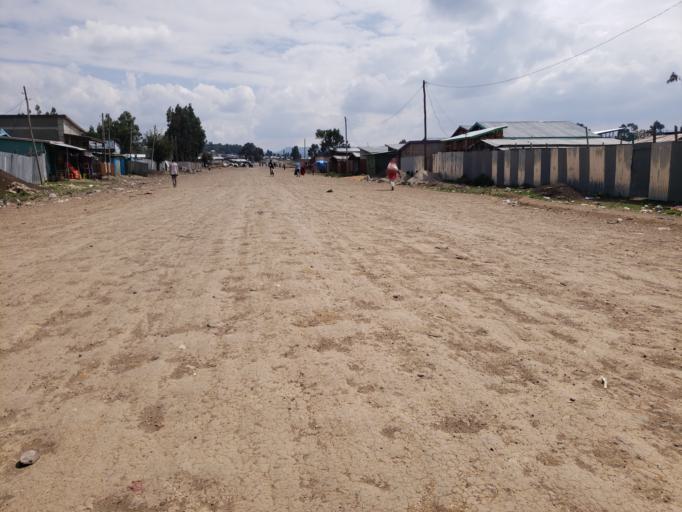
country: ET
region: Oromiya
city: Dodola
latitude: 7.0031
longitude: 39.3917
